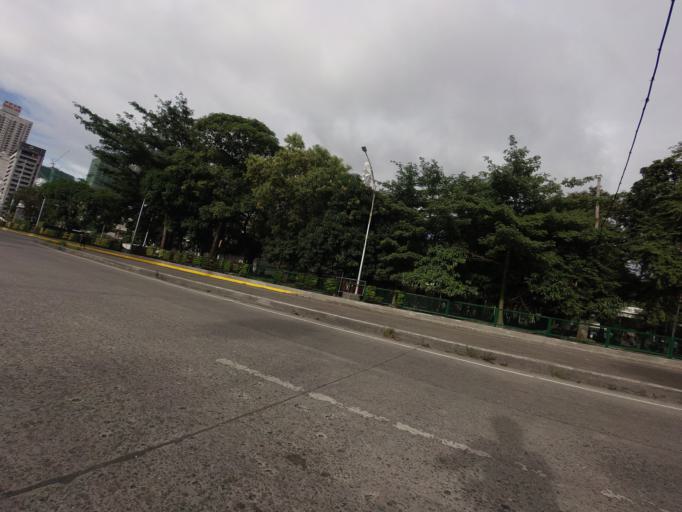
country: PH
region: Metro Manila
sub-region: City of Manila
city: Quiapo
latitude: 14.5938
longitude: 120.9784
